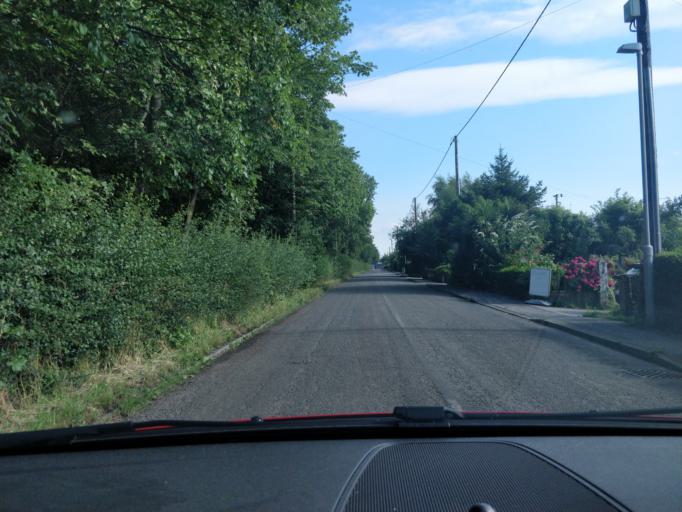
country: GB
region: England
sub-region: Lancashire
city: Banks
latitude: 53.6692
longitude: -2.9198
